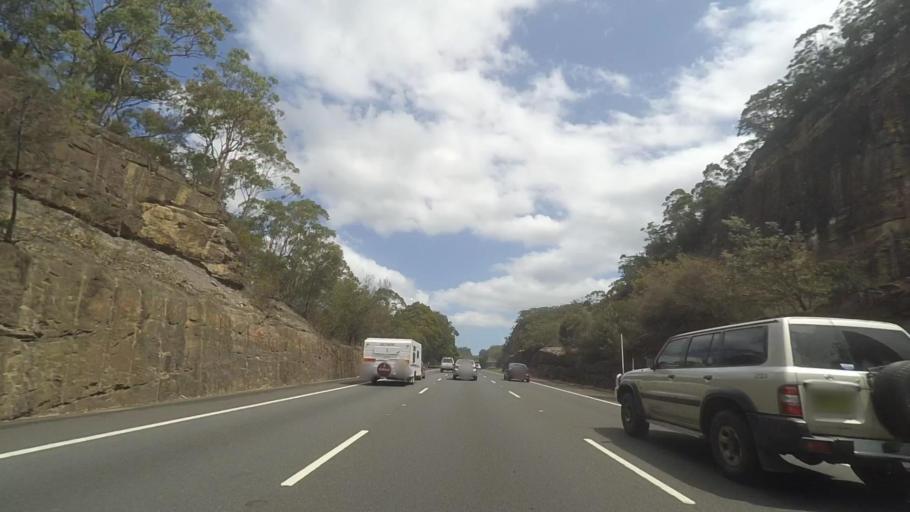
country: AU
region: New South Wales
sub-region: Hornsby Shire
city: Berowra
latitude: -33.5537
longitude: 151.1926
